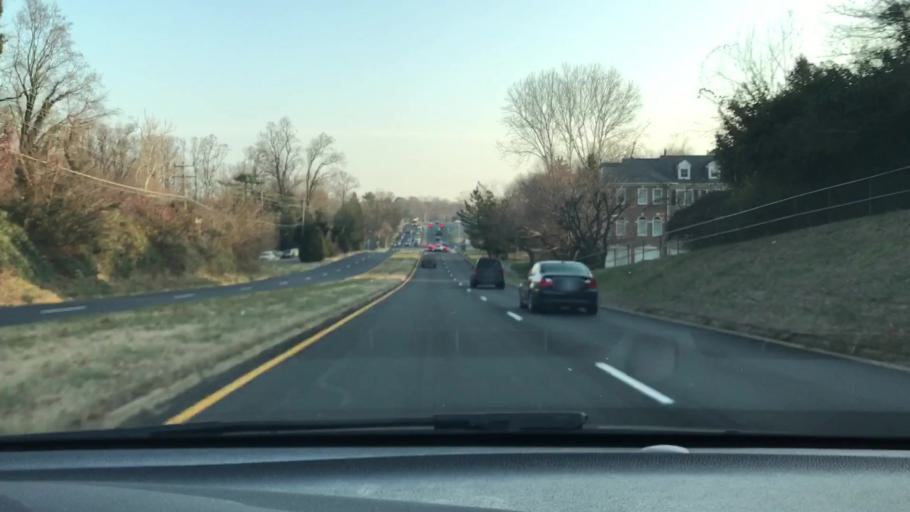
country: US
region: Virginia
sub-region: Fairfax County
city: Lake Barcroft
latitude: 38.8380
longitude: -77.1545
